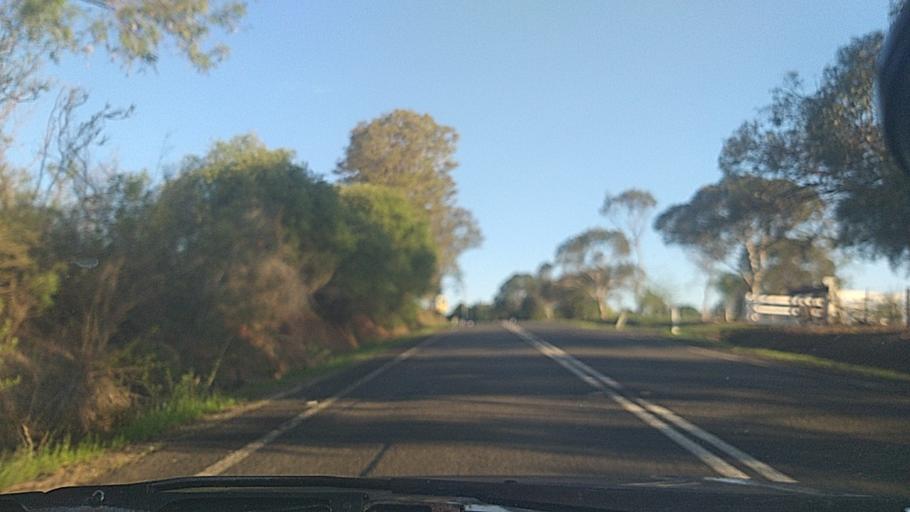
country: AU
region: New South Wales
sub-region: Wollondilly
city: Douglas Park
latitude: -34.1458
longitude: 150.7193
